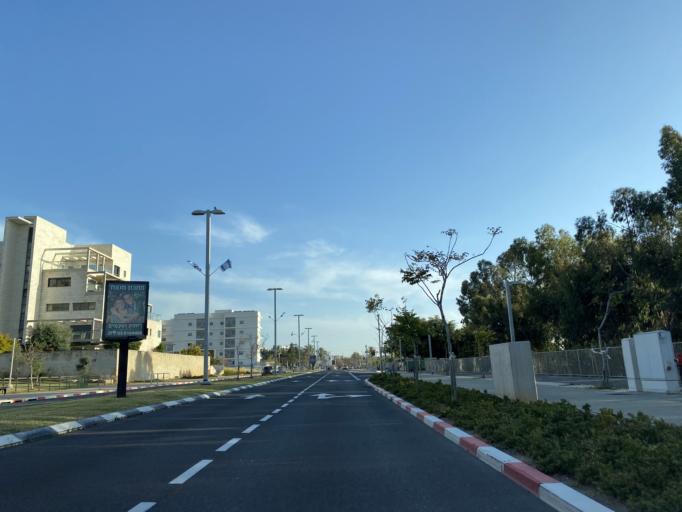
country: IL
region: Tel Aviv
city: Herzliyya
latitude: 32.1738
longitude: 34.8293
